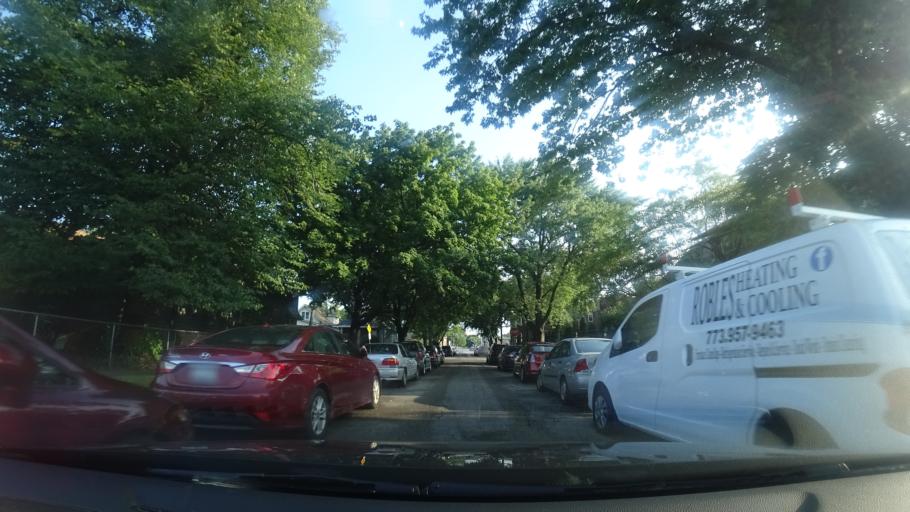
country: US
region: Illinois
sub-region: Cook County
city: Elmwood Park
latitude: 41.9374
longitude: -87.7494
